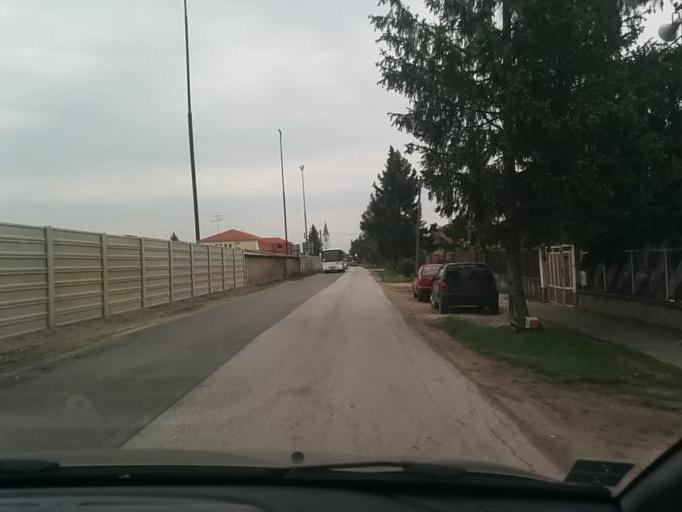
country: SK
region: Trnavsky
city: Sladkovicovo
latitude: 48.2048
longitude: 17.6346
